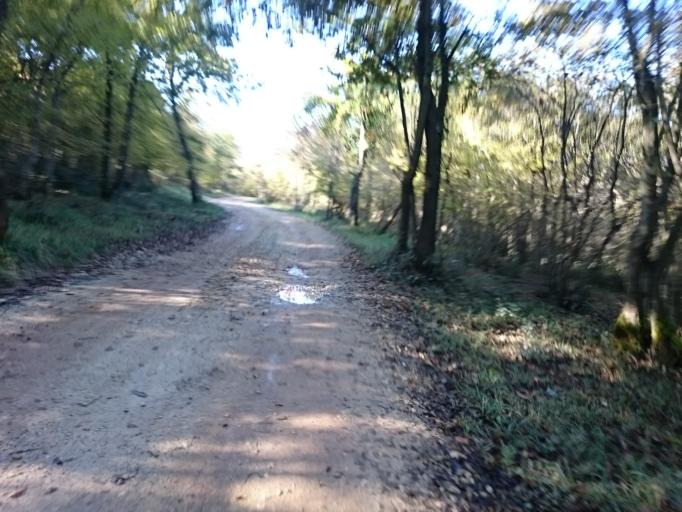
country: HR
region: Istarska
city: Novigrad
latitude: 45.2851
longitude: 13.6027
